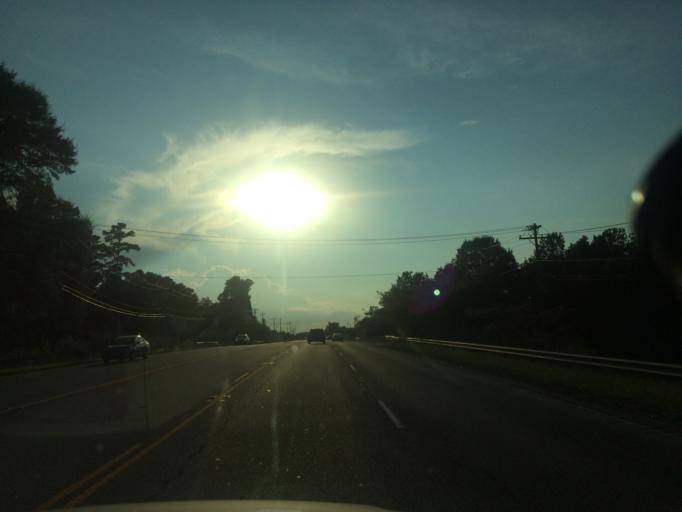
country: US
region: South Carolina
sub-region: Spartanburg County
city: Fairforest
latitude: 34.9378
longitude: -82.0269
